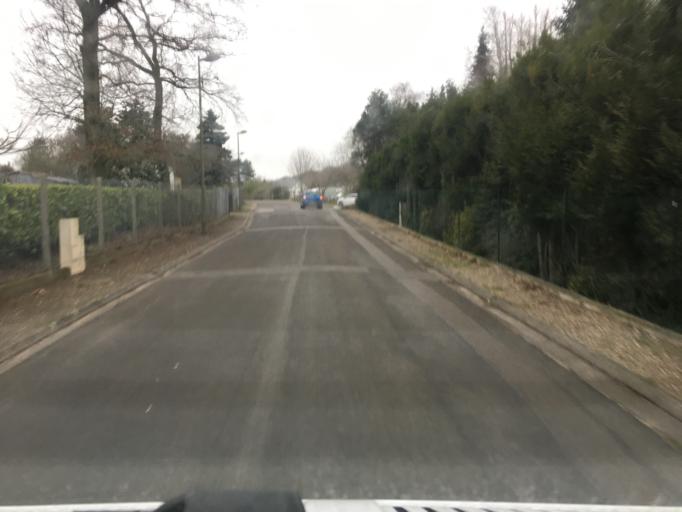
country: FR
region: Picardie
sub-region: Departement de la Somme
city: Saint-Valery-sur-Somme
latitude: 50.1817
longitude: 1.6302
